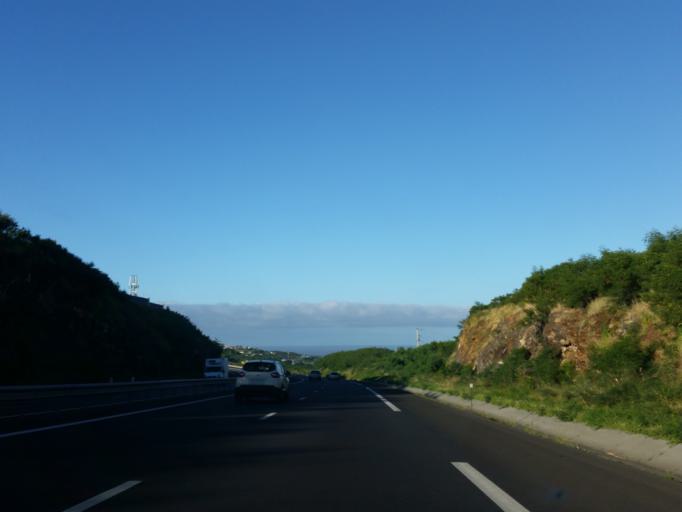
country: RE
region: Reunion
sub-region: Reunion
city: Saint-Leu
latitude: -21.1785
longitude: 55.2966
